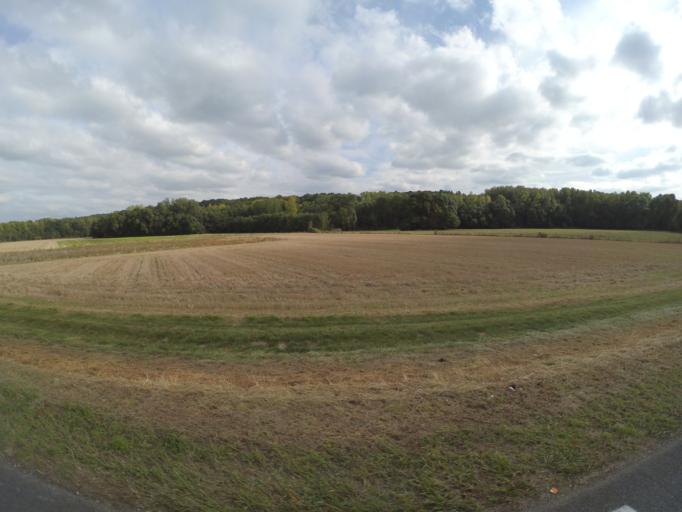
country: FR
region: Centre
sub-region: Departement d'Indre-et-Loire
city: Vernou-sur-Brenne
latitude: 47.4309
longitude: 0.8513
